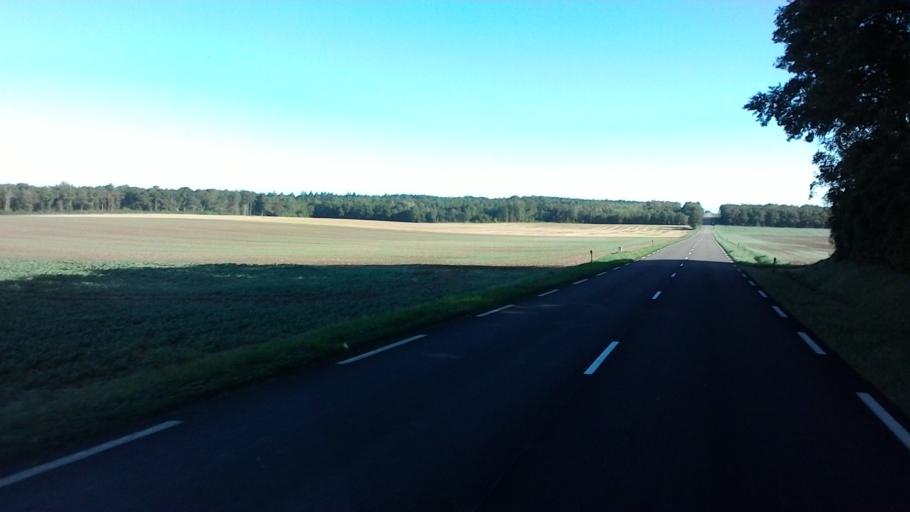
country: FR
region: Bourgogne
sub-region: Departement de la Cote-d'Or
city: Montbard
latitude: 47.6827
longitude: 4.4071
